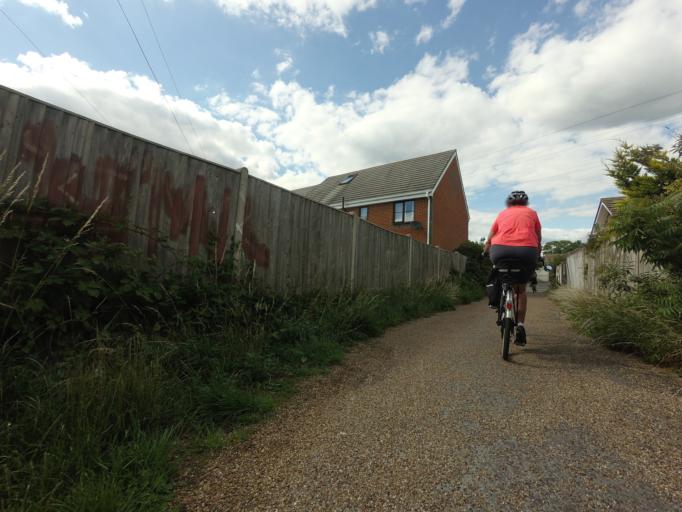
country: GB
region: England
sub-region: East Sussex
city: Hailsham
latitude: 50.8199
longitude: 0.2616
